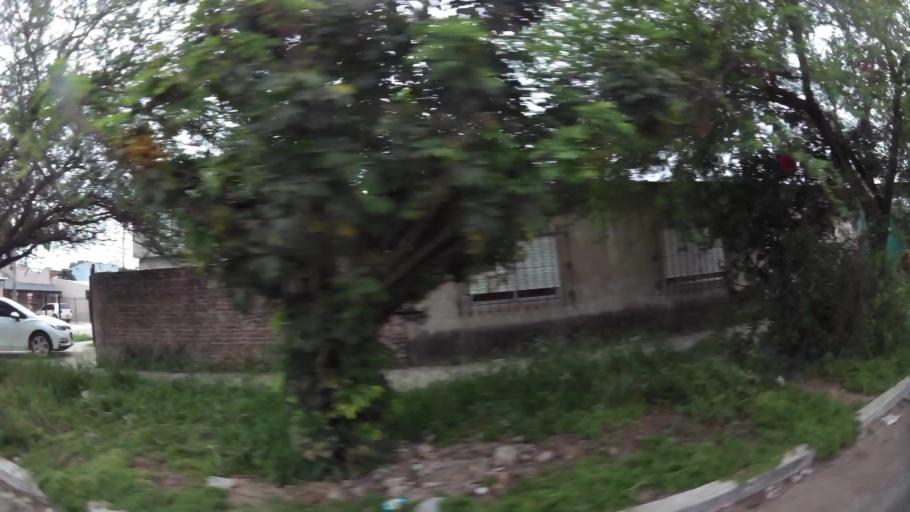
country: AR
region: Buenos Aires
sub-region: Partido de Zarate
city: Zarate
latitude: -34.1134
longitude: -59.0281
